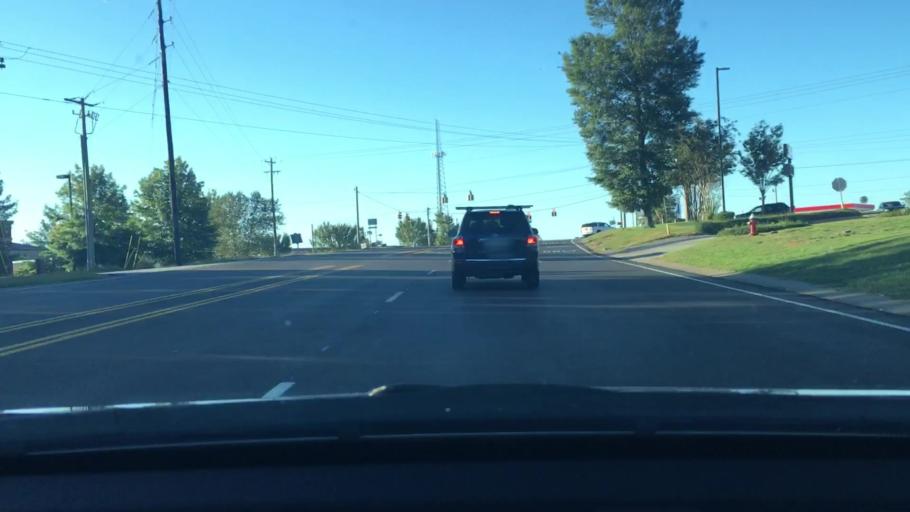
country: US
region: South Carolina
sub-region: Lexington County
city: Irmo
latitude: 34.0976
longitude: -81.1603
